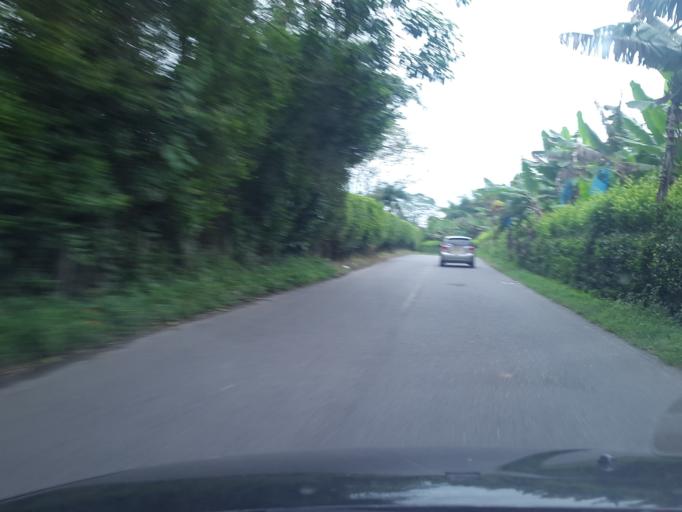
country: CO
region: Quindio
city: La Tebaida
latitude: 4.4883
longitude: -75.7984
